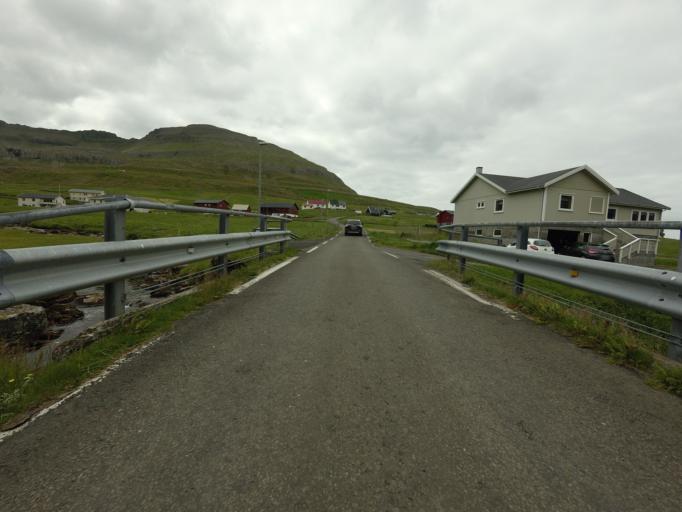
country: FO
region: Suduroy
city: Tvoroyri
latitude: 61.5225
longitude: -6.8796
